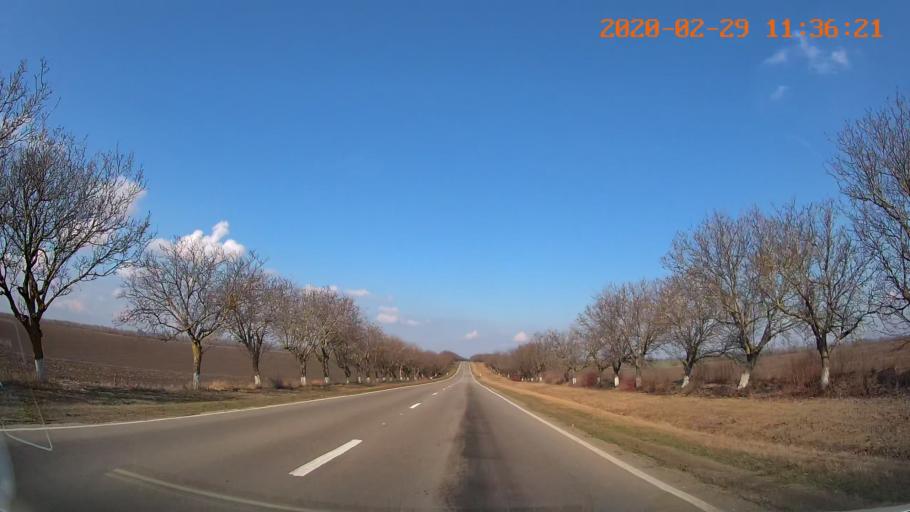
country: MD
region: Rezina
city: Saharna
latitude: 47.5947
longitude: 29.0566
